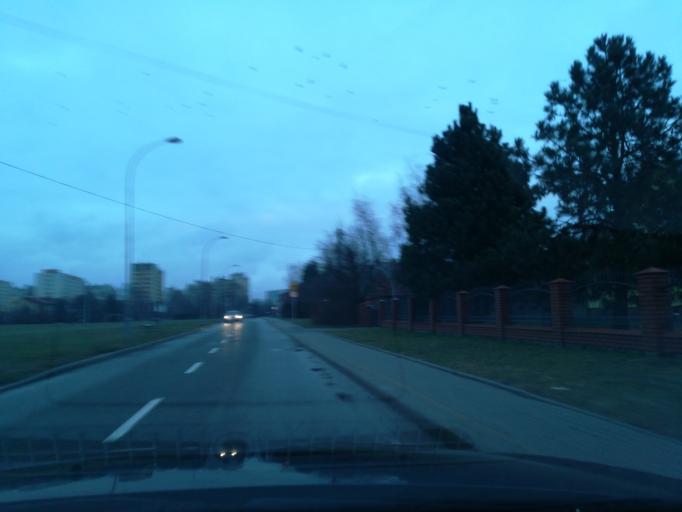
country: PL
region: Subcarpathian Voivodeship
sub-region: Rzeszow
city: Rzeszow
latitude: 50.0134
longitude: 22.0054
